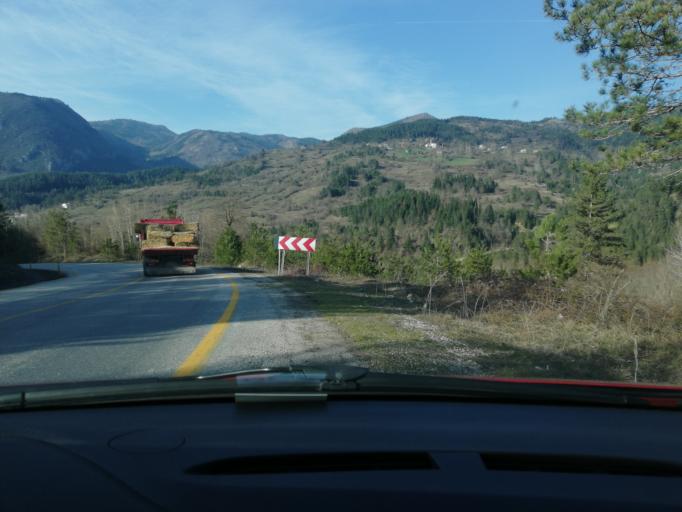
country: TR
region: Kastamonu
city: Senpazar
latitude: 41.7879
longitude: 33.1742
